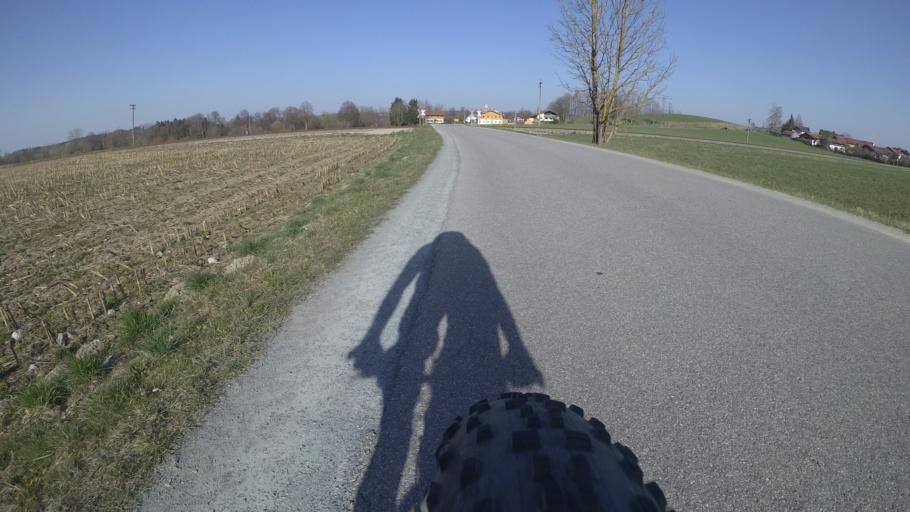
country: DE
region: Bavaria
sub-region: Upper Bavaria
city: Traunreut
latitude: 47.9398
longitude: 12.5843
